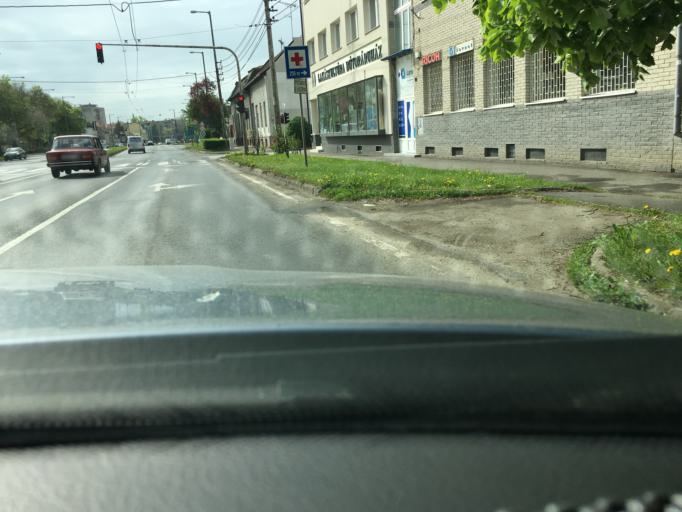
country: HU
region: Hajdu-Bihar
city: Debrecen
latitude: 47.5251
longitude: 21.6179
